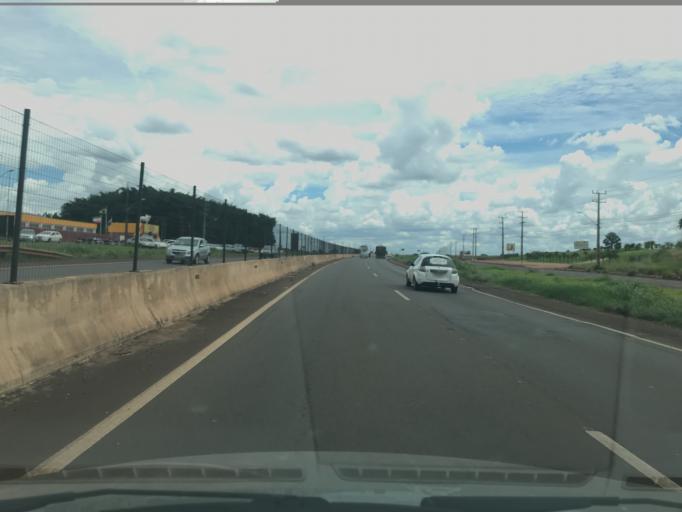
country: BR
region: Parana
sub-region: Paicandu
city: Paicandu
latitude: -23.4539
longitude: -52.0118
